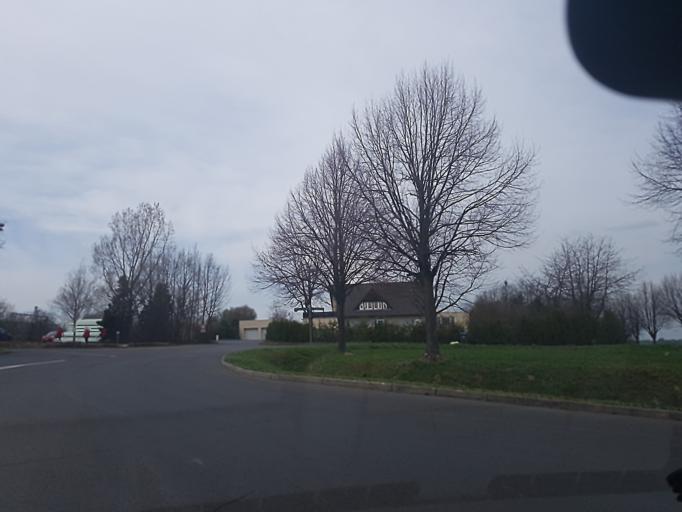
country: DE
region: Saxony
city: Mugeln
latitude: 51.2297
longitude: 13.0212
